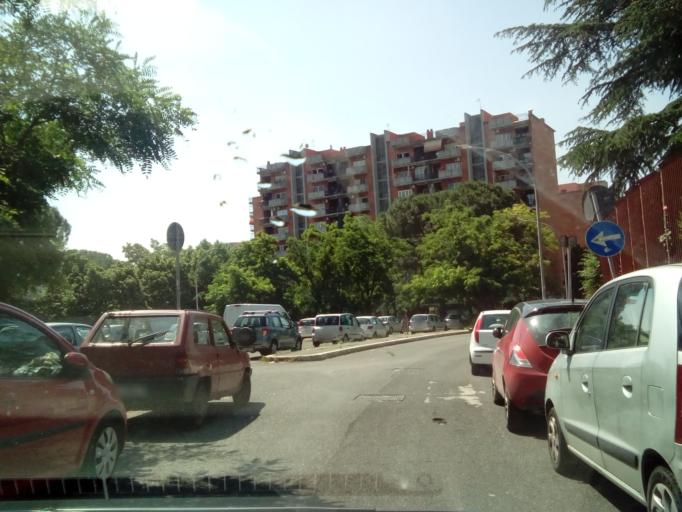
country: IT
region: Latium
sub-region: Citta metropolitana di Roma Capitale
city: Rome
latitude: 41.8884
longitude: 12.5843
